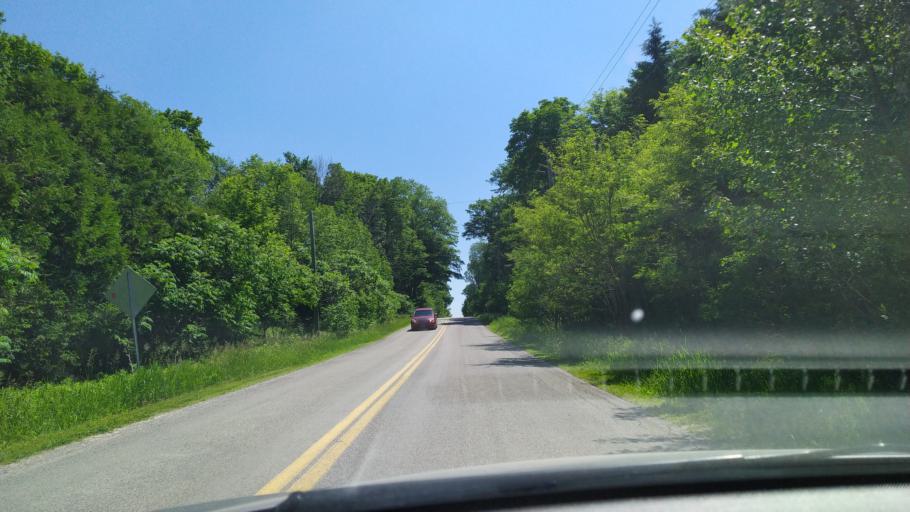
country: CA
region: Ontario
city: Waterloo
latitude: 43.4725
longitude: -80.6277
